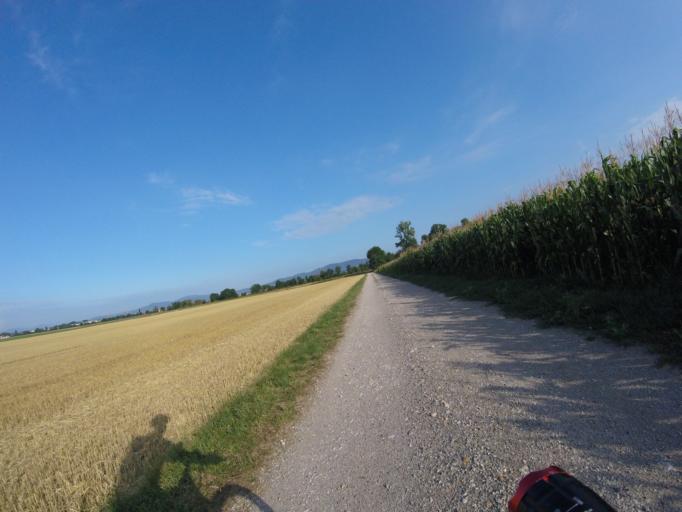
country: AT
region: Lower Austria
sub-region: Politischer Bezirk Baden
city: Trumau
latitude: 48.0028
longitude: 16.3645
